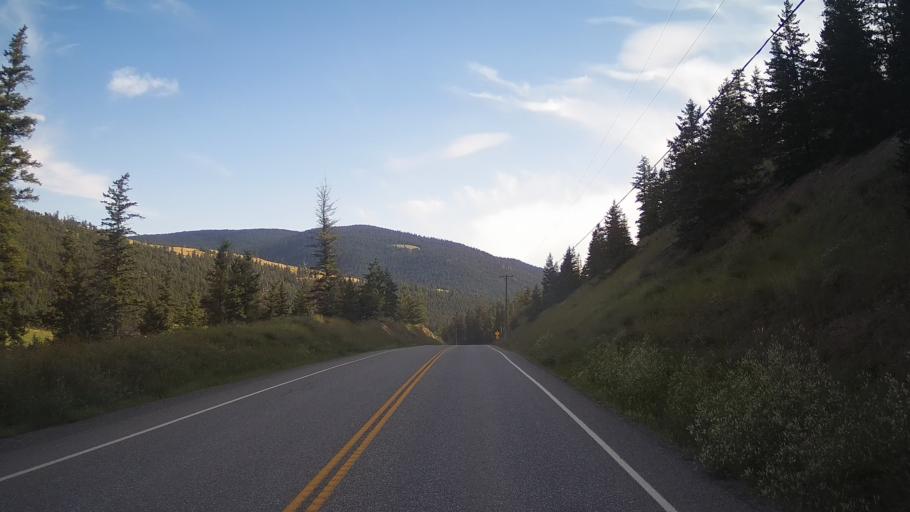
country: CA
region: British Columbia
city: Cache Creek
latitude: 50.8468
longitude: -121.5393
